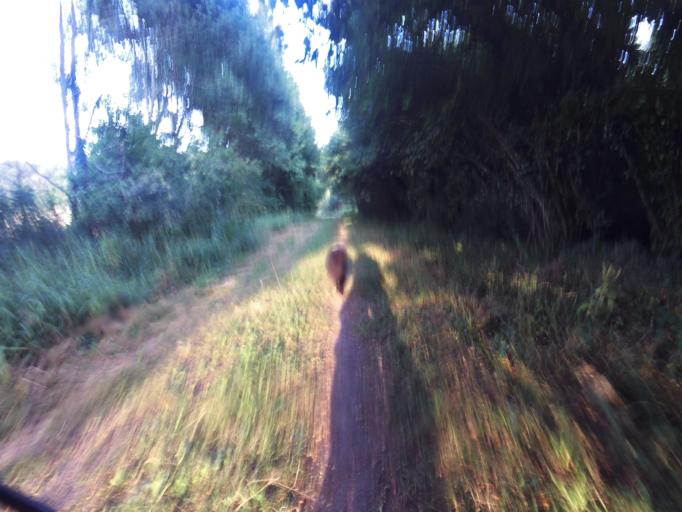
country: FR
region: Brittany
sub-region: Departement du Morbihan
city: Molac
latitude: 47.7171
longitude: -2.4256
